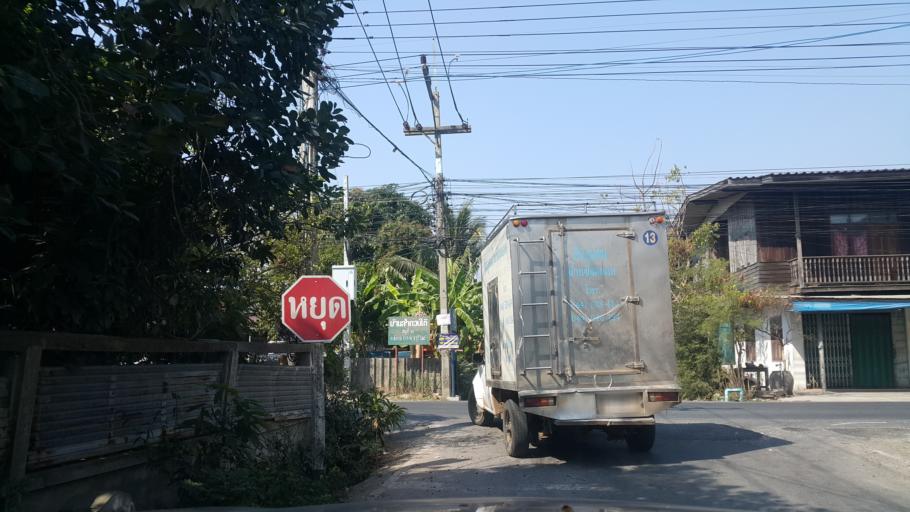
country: TH
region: Buriram
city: Krasang
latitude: 15.0541
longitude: 103.3837
